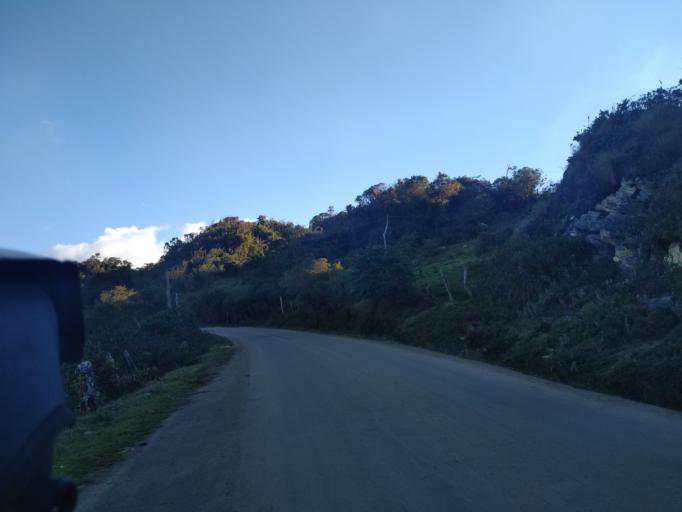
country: PE
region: Amazonas
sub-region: Provincia de Chachapoyas
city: Montevideo
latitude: -6.7173
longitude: -77.8652
